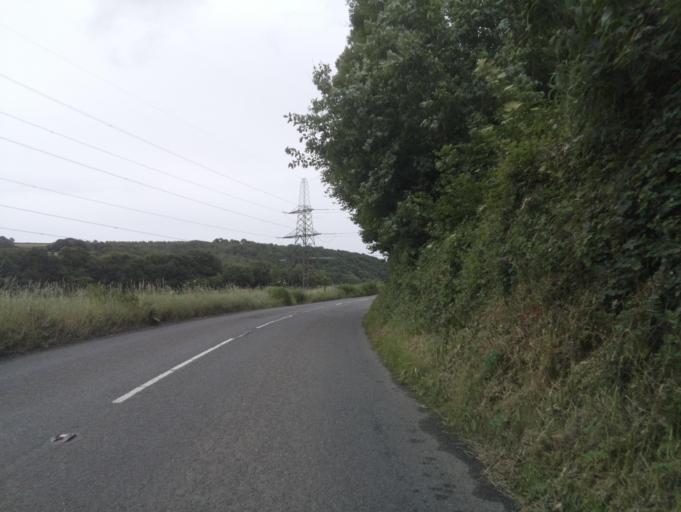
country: GB
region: England
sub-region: Devon
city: Chudleigh
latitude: 50.6129
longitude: -3.6225
